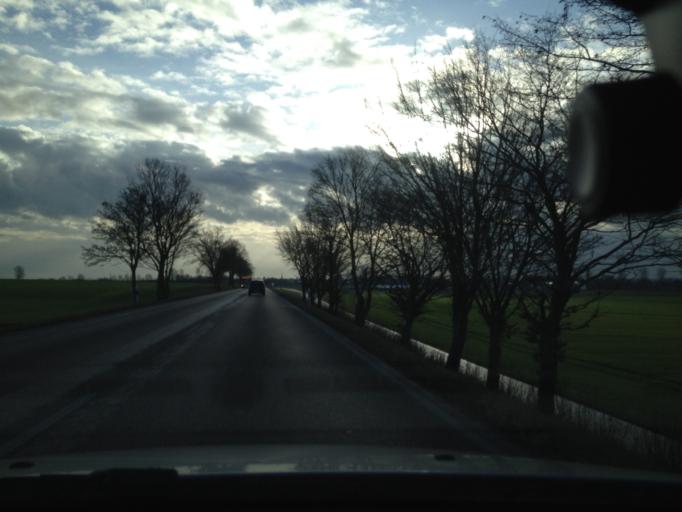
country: DE
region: Bavaria
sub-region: Swabia
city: Grossaitingen
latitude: 48.2159
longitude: 10.7759
